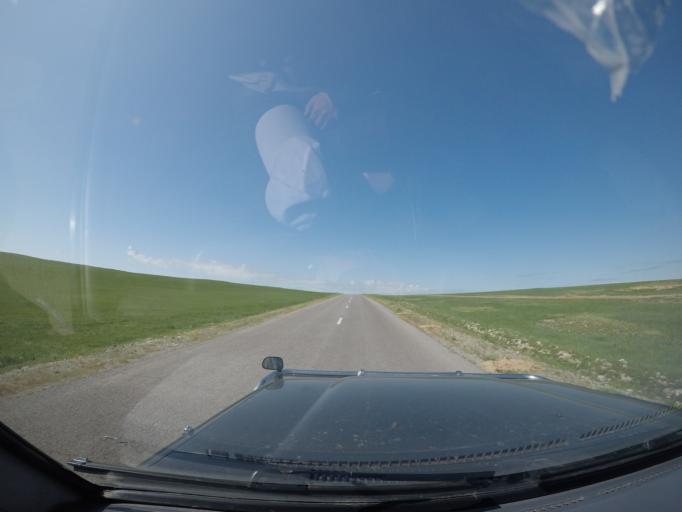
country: MN
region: Suhbaatar
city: Bayasgalant
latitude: 47.3519
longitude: 111.6479
